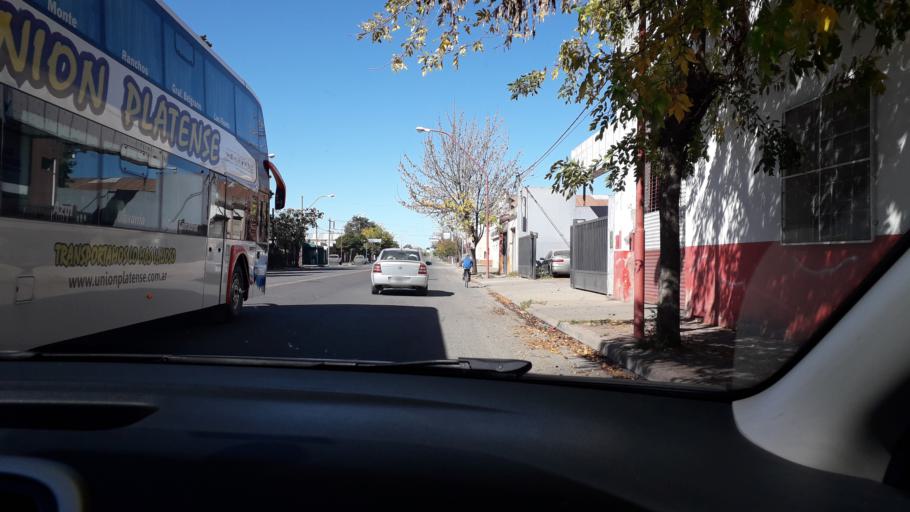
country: AR
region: Buenos Aires
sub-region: Partido de Azul
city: Azul
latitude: -36.7875
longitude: -59.8464
